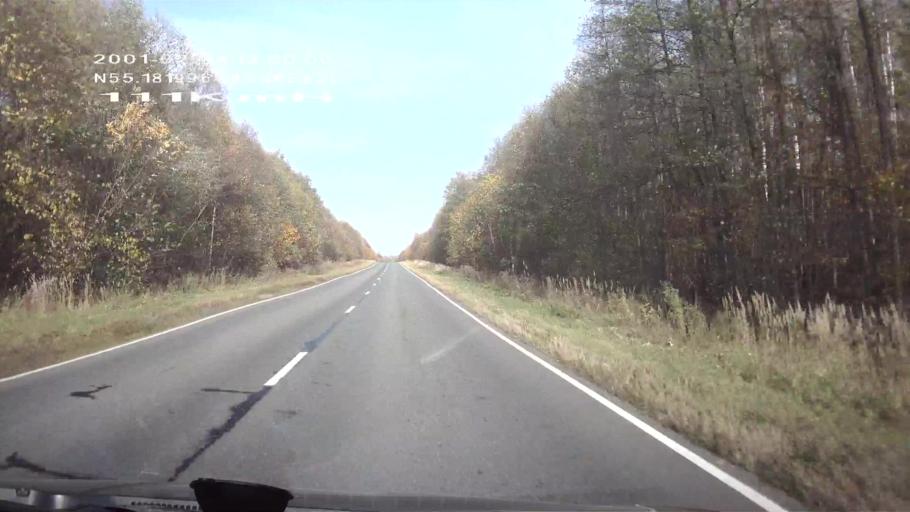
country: RU
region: Chuvashia
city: Buinsk
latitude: 55.1821
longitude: 47.0659
